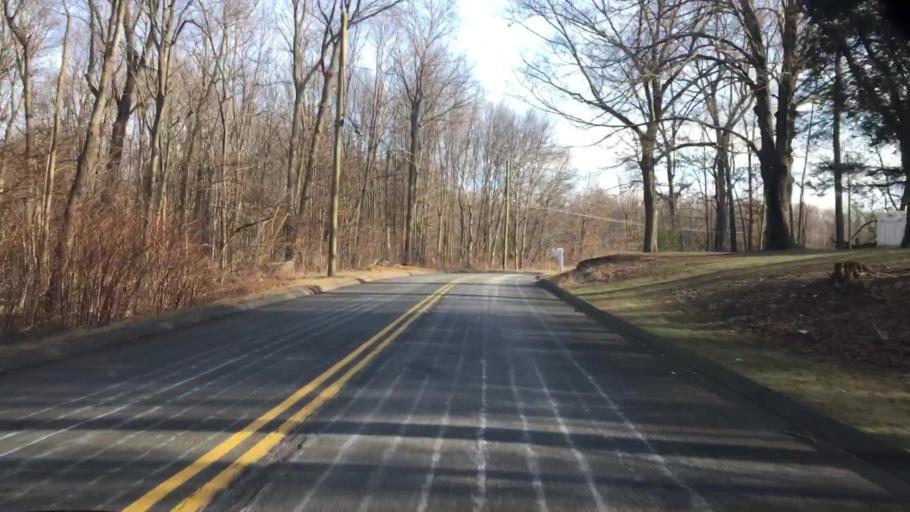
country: US
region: Connecticut
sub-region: New Haven County
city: Prospect
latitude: 41.5325
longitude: -72.9639
